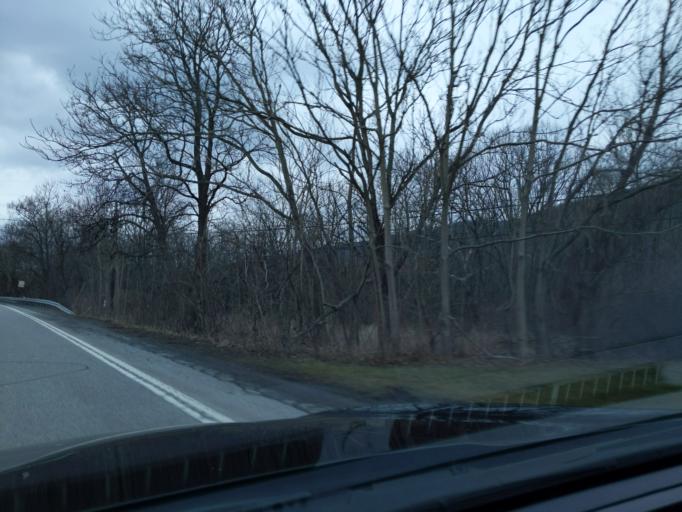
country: US
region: Pennsylvania
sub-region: Blair County
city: Tipton
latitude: 40.6369
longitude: -78.2829
